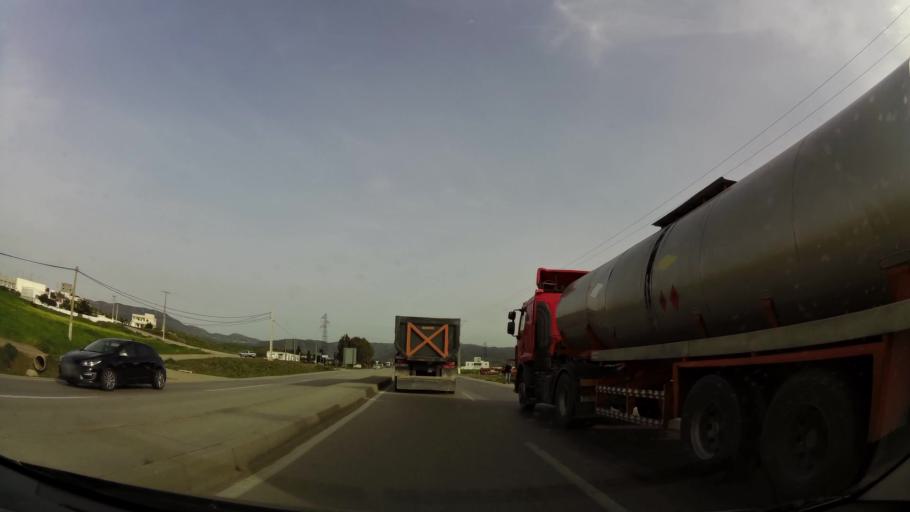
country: MA
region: Tanger-Tetouan
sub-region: Tanger-Assilah
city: Dar Chaoui
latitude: 35.5829
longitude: -5.6388
